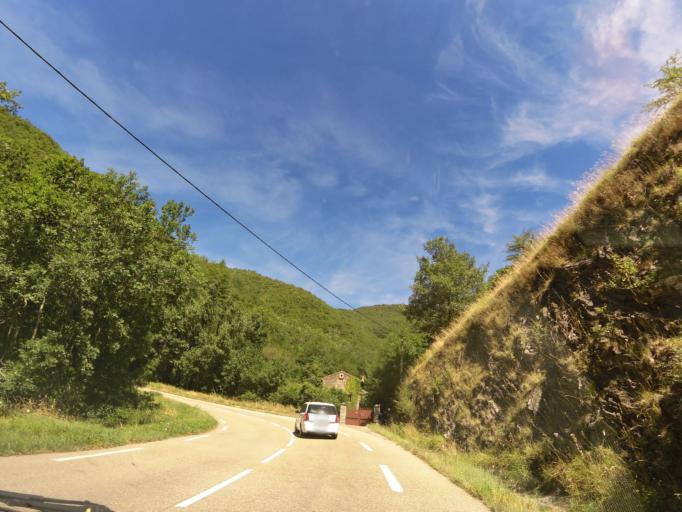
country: FR
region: Languedoc-Roussillon
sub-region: Departement du Gard
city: Le Vigan
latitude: 43.9811
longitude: 3.4689
